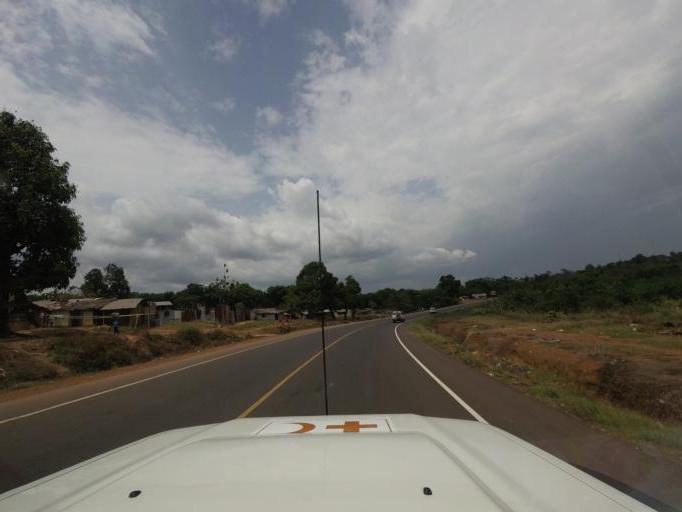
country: LR
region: Margibi
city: Kakata
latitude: 6.5318
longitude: -10.3729
